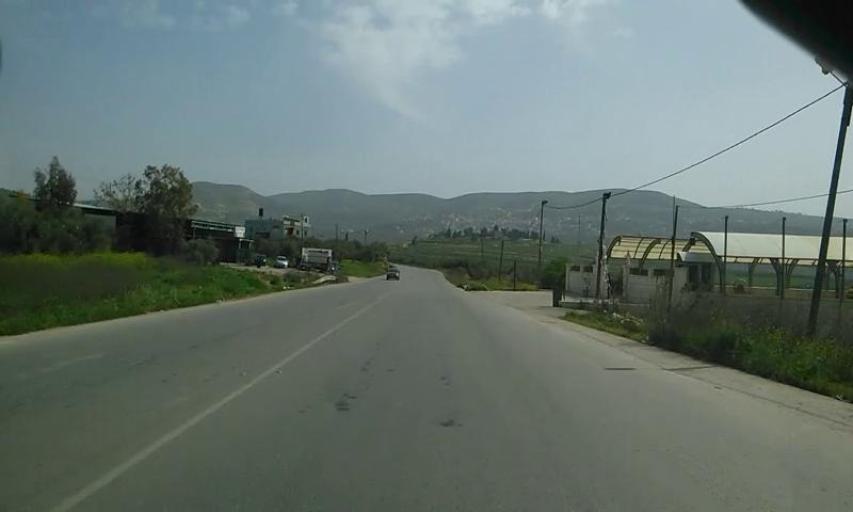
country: PS
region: West Bank
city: `Ajjah
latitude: 32.3458
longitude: 35.2012
